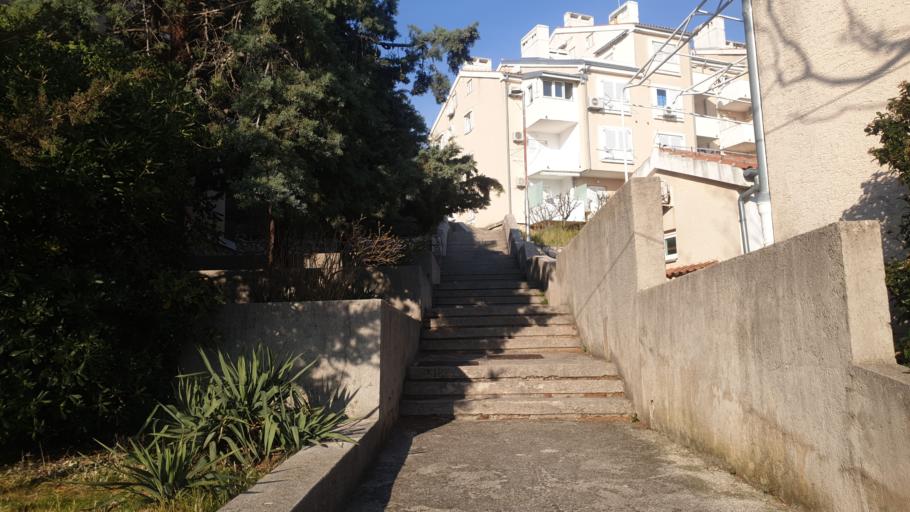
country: HR
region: Primorsko-Goranska
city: Novi Vinodolski
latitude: 45.1275
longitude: 14.7966
